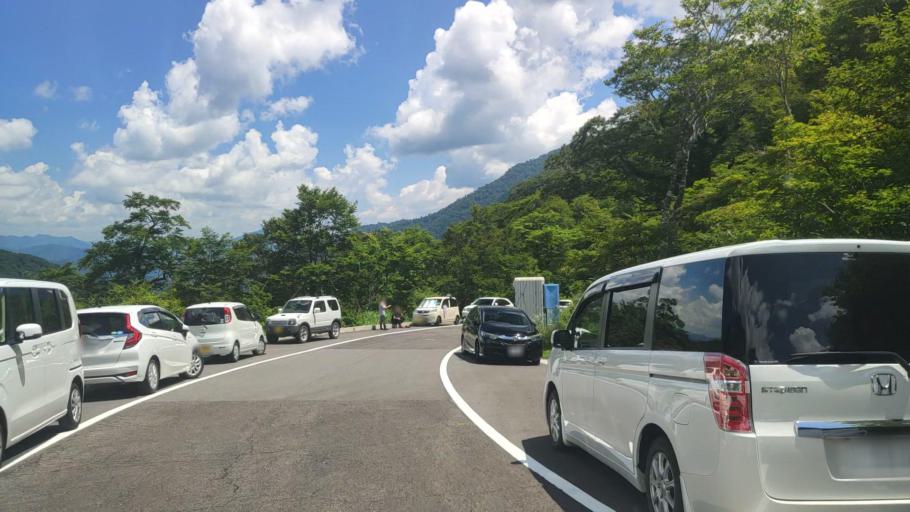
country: JP
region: Fukui
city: Ono
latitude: 35.7791
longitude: 136.5188
